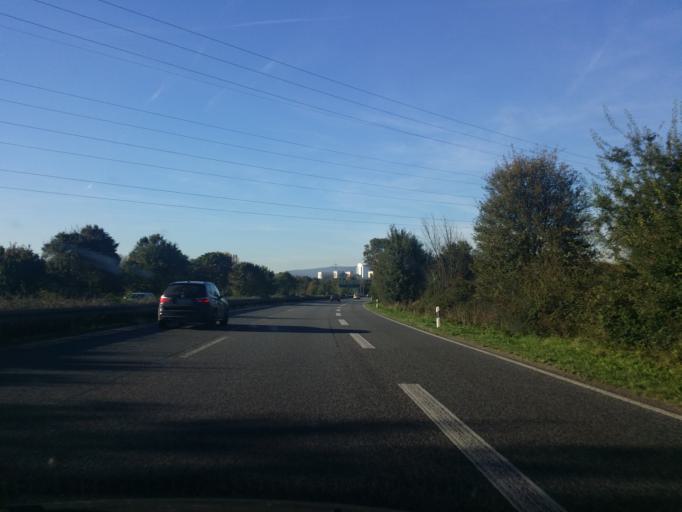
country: DE
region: Hesse
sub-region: Regierungsbezirk Darmstadt
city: Eschborn
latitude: 50.1184
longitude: 8.5863
